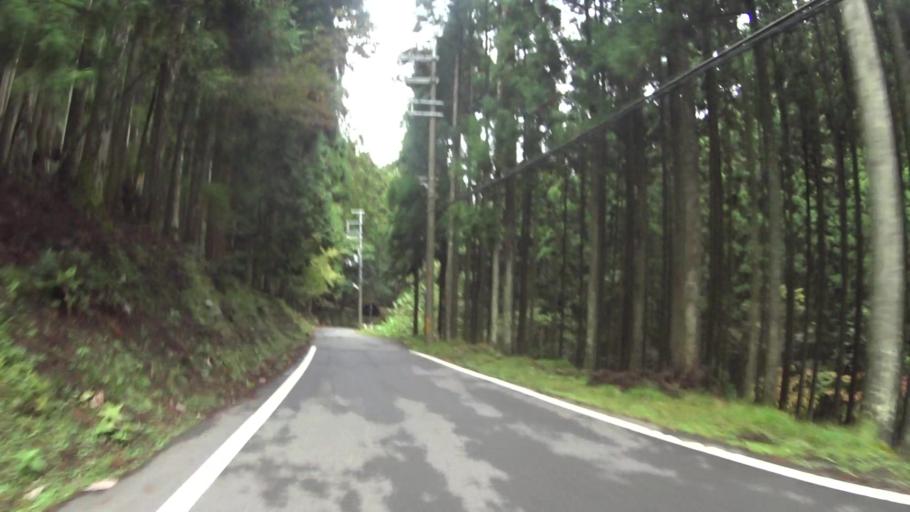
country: JP
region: Shiga Prefecture
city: Kitahama
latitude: 35.1854
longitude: 135.7836
